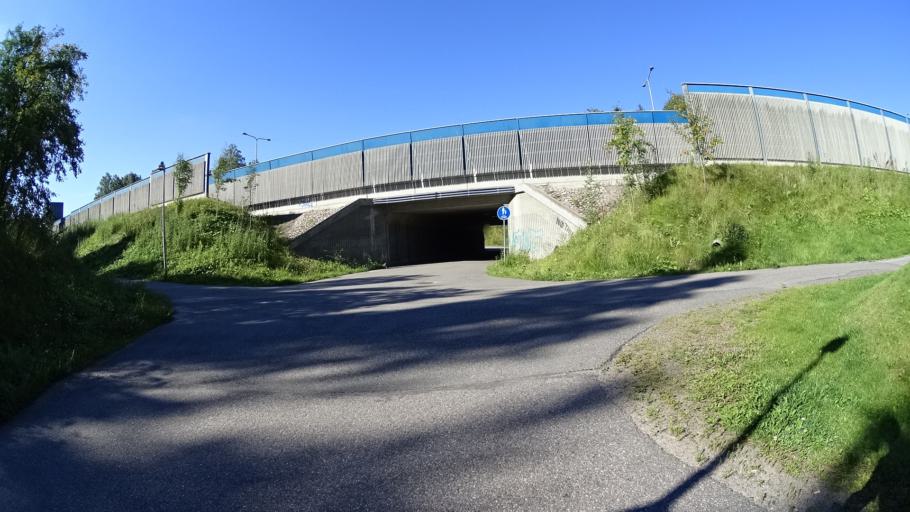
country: FI
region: Uusimaa
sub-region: Helsinki
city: Teekkarikylae
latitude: 60.2848
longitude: 24.8652
